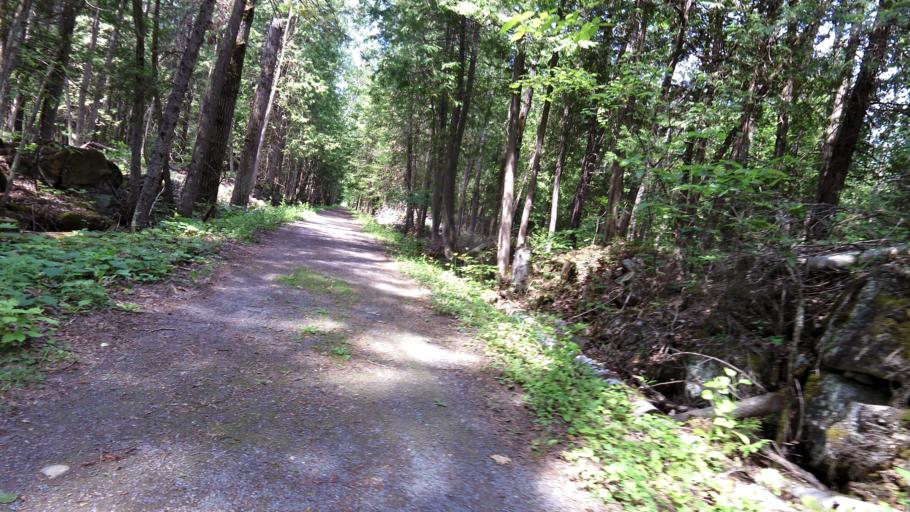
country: CA
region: Ontario
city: Arnprior
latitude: 45.4597
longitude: -76.2584
